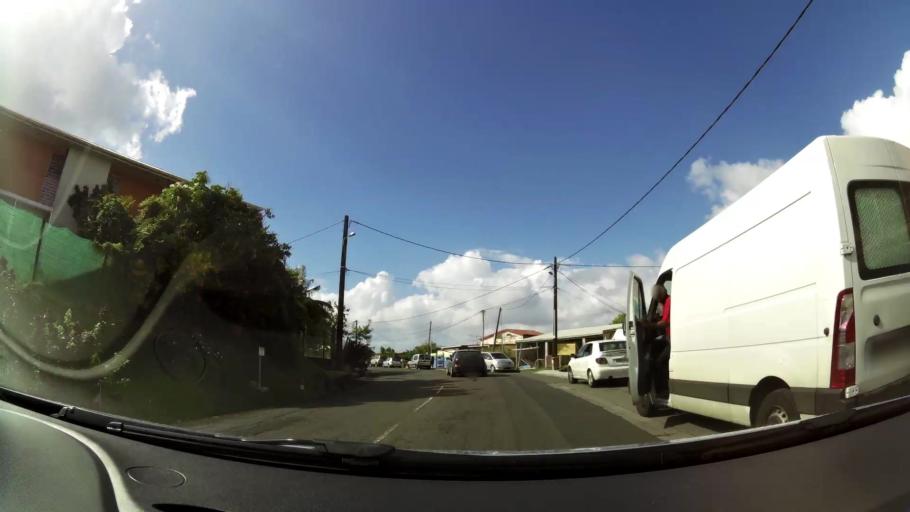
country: MQ
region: Martinique
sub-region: Martinique
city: Les Trois-Ilets
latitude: 14.5406
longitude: -61.0382
